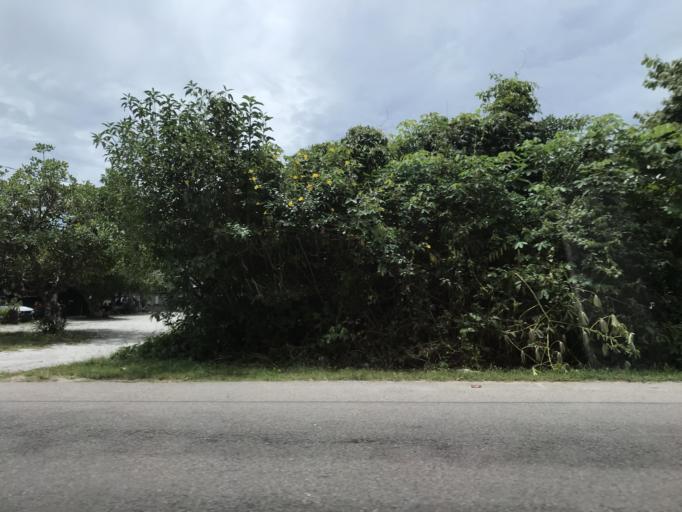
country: MY
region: Kelantan
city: Tumpat
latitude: 6.1785
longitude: 102.1836
